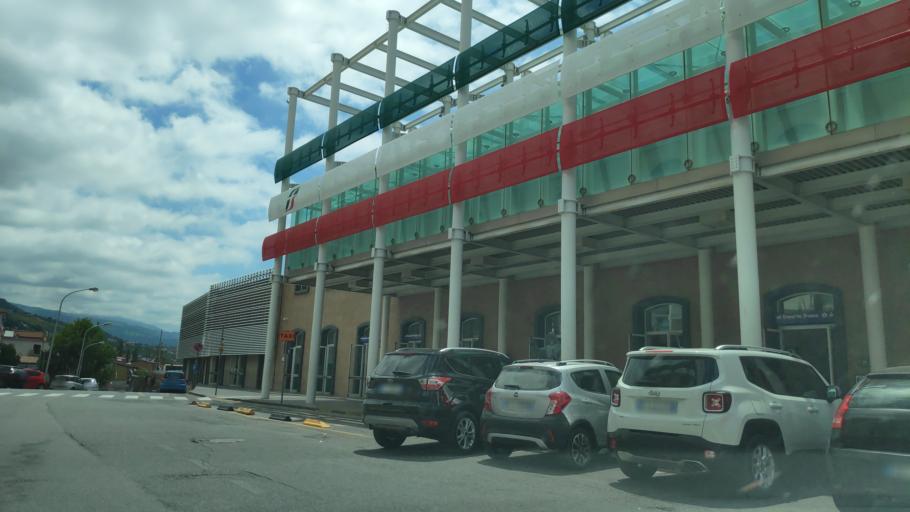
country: IT
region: Calabria
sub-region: Provincia di Cosenza
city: Paola
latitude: 39.3597
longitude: 16.0334
